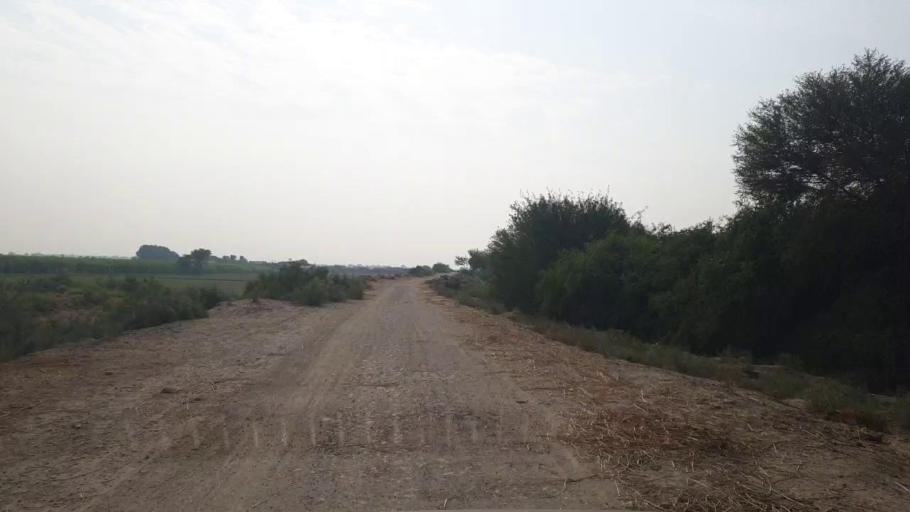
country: PK
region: Sindh
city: Tando Muhammad Khan
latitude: 25.1278
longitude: 68.4908
